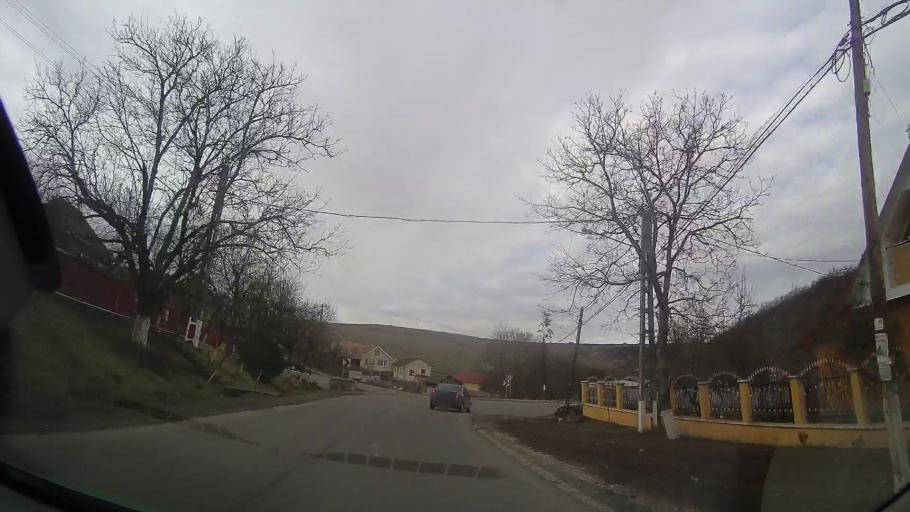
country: RO
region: Bistrita-Nasaud
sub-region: Comuna Silvasu de Campie
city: Silvasu de Campie
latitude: 46.7829
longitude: 24.2906
